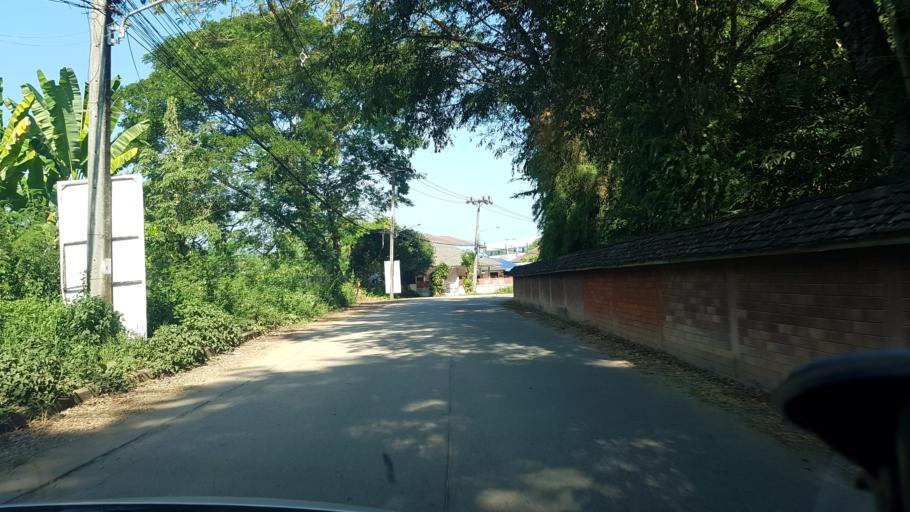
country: TH
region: Chiang Rai
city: Chiang Rai
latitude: 19.9032
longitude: 99.7931
